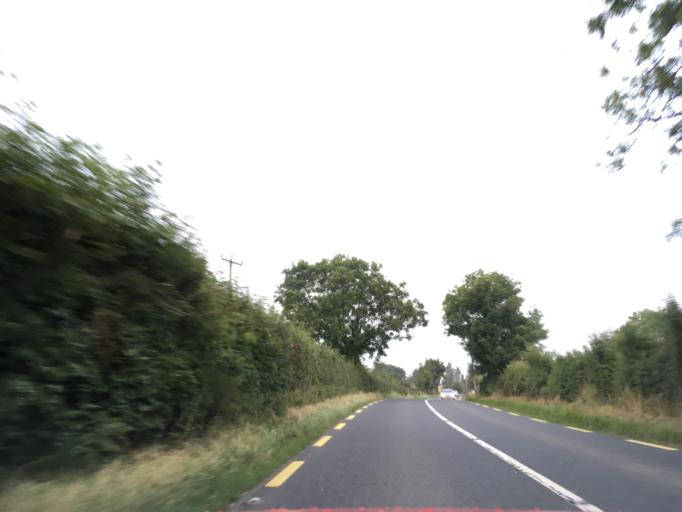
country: IE
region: Munster
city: Cashel
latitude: 52.4953
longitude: -8.0021
